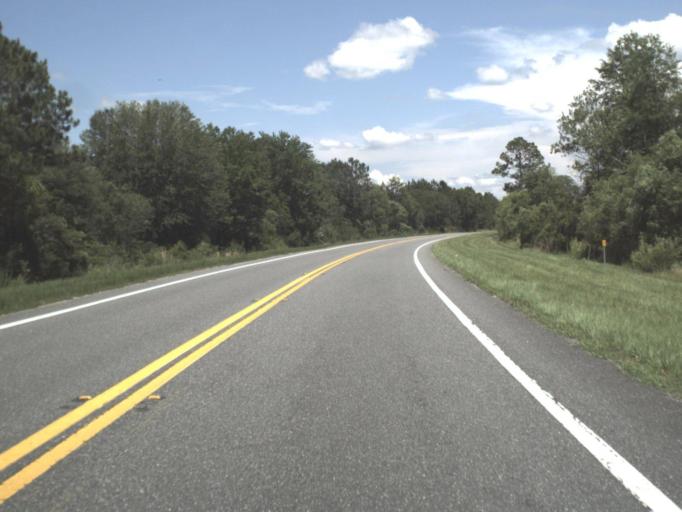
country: US
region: Florida
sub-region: Lafayette County
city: Mayo
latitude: 30.1291
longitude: -83.3616
